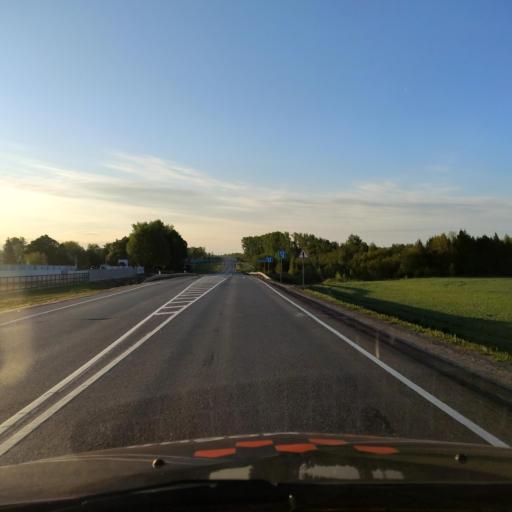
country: RU
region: Orjol
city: Livny
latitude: 52.4440
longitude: 37.5349
